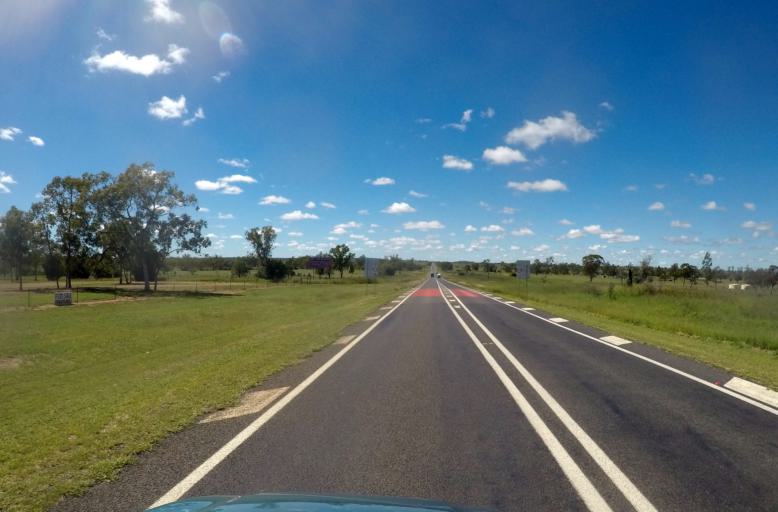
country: AU
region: Queensland
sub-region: Western Downs
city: Westcourt
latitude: -26.6446
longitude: 149.7685
